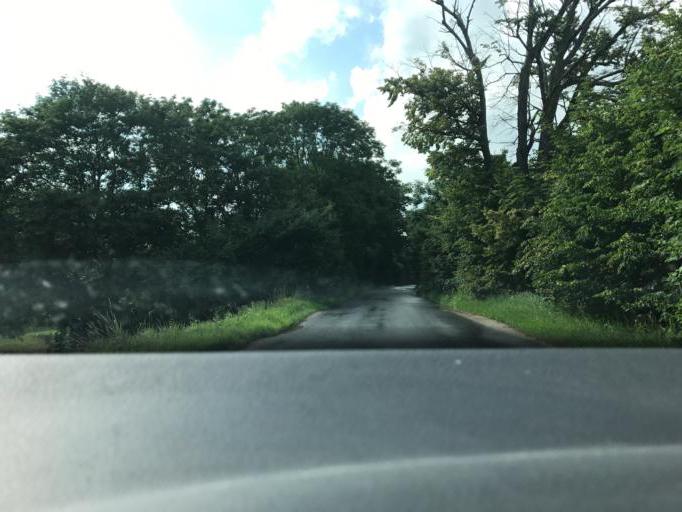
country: PL
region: Pomeranian Voivodeship
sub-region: Powiat gdanski
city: Cedry Wielkie
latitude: 54.3391
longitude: 18.8001
